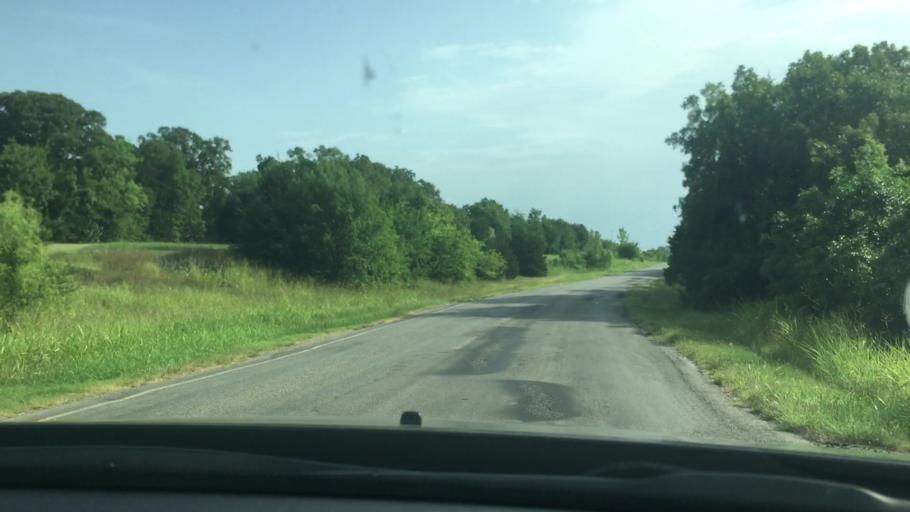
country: US
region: Oklahoma
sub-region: Pontotoc County
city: Byng
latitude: 34.8670
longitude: -96.5992
